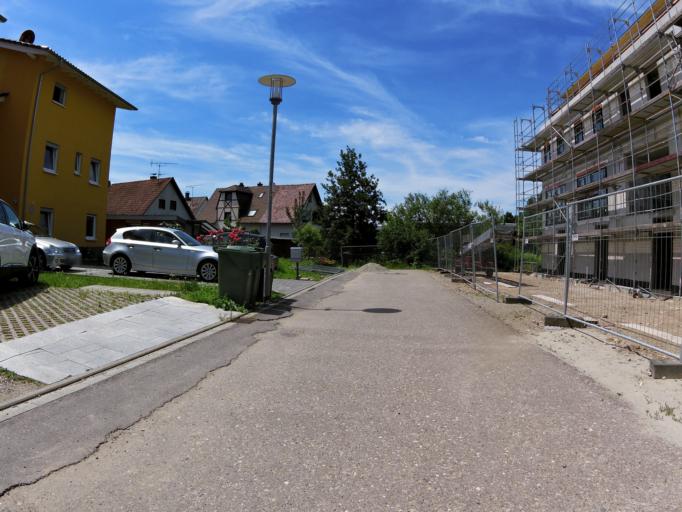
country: DE
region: Baden-Wuerttemberg
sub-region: Freiburg Region
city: Lahr
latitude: 48.3353
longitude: 7.8565
